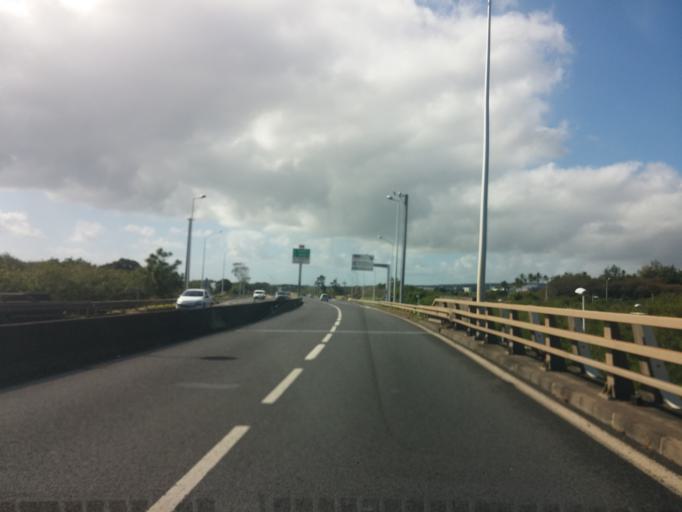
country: RE
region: Reunion
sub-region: Reunion
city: Sainte-Marie
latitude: -20.8959
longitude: 55.5038
